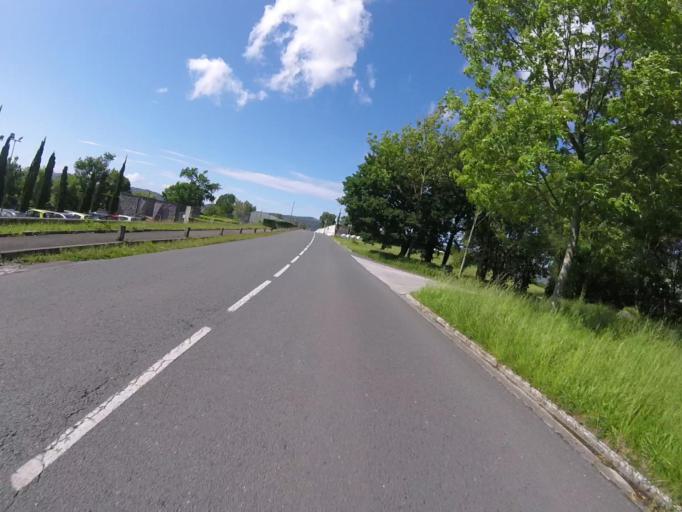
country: ES
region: Basque Country
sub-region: Provincia de Guipuzcoa
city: Errenteria
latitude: 43.2980
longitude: -1.8924
